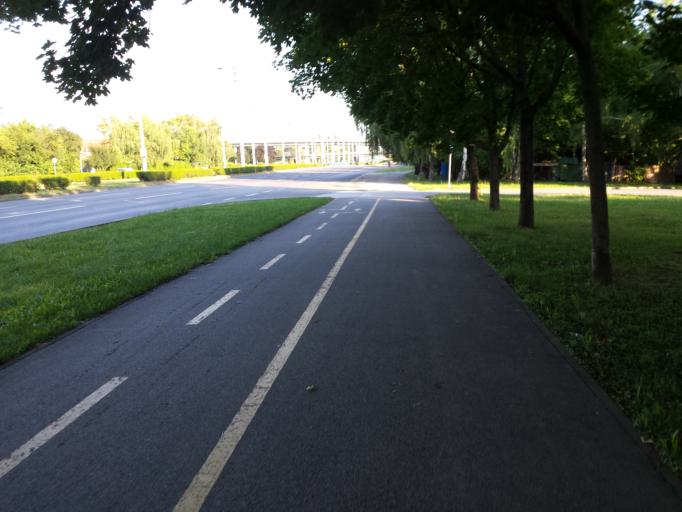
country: HR
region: Grad Zagreb
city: Novi Zagreb
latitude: 45.7985
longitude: 15.9970
